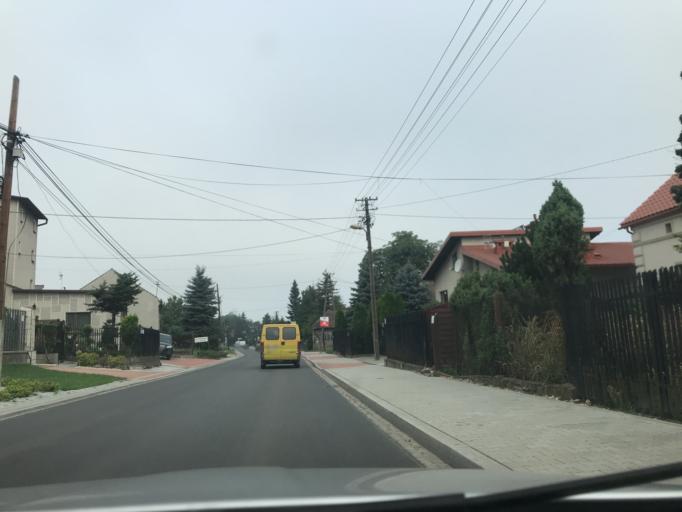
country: PL
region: Lesser Poland Voivodeship
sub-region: Powiat krakowski
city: Ochojno
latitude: 50.0069
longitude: 19.9784
